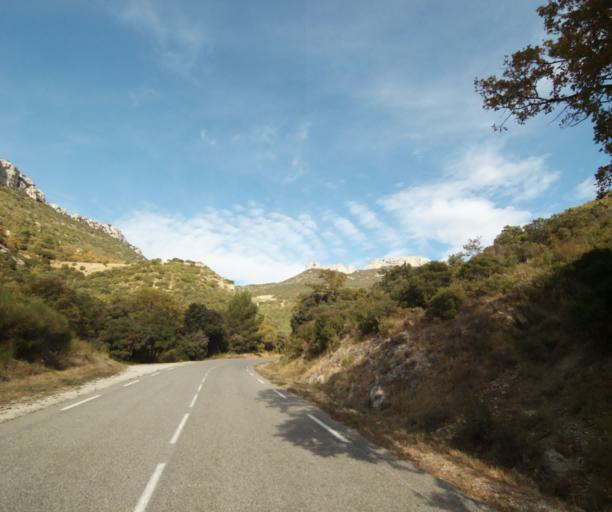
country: FR
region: Provence-Alpes-Cote d'Azur
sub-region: Departement des Bouches-du-Rhone
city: Gemenos
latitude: 43.3054
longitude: 5.6682
